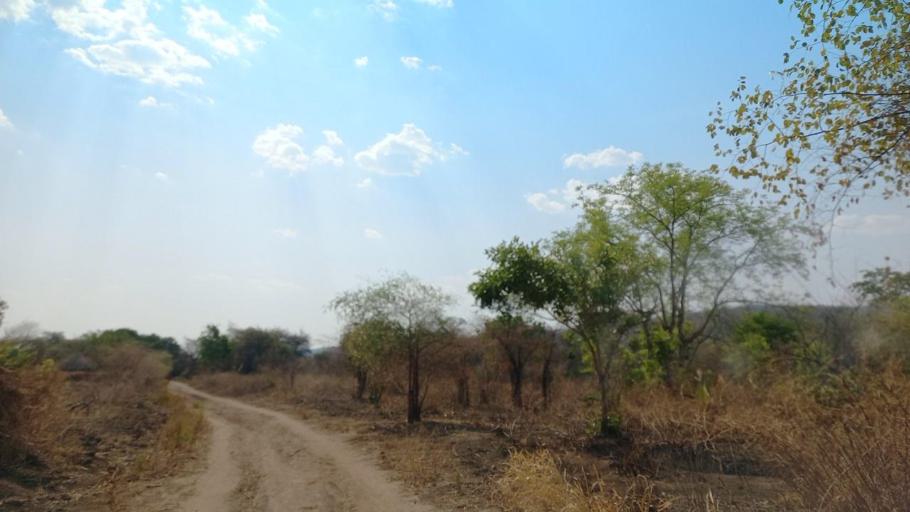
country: ZM
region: Lusaka
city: Luangwa
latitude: -15.0912
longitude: 30.1504
